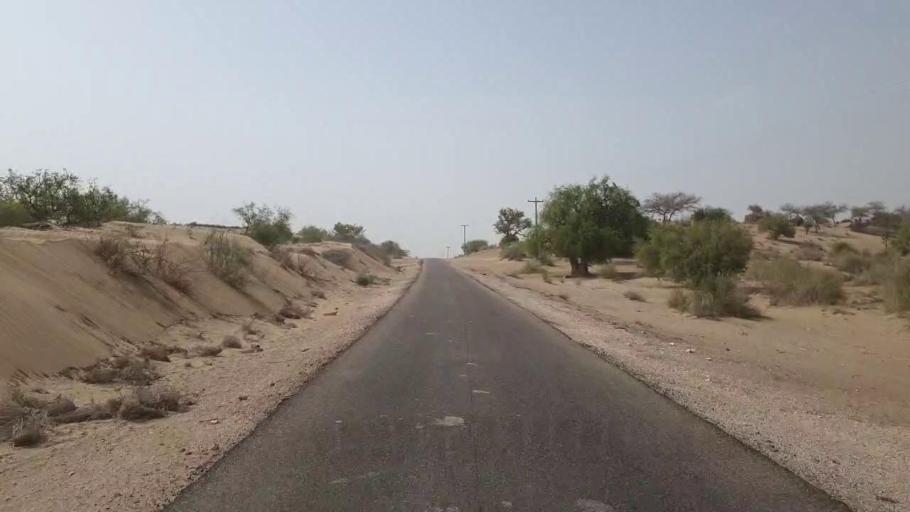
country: PK
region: Sindh
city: Mithi
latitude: 24.5977
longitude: 69.9246
